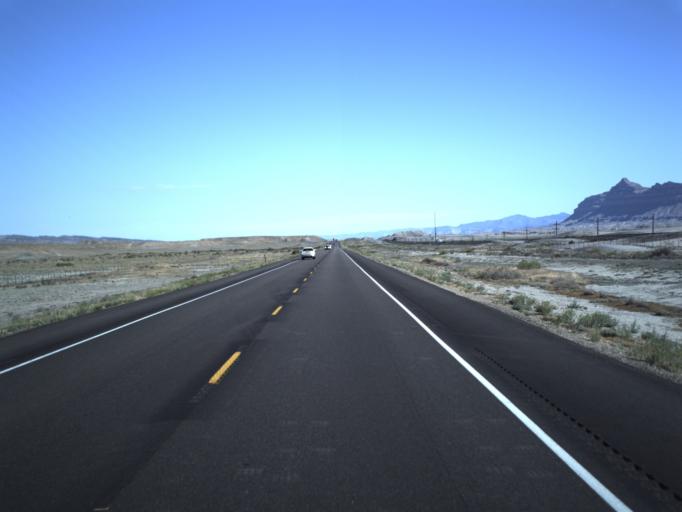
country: US
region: Utah
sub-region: Carbon County
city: East Carbon City
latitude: 39.0728
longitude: -110.3159
